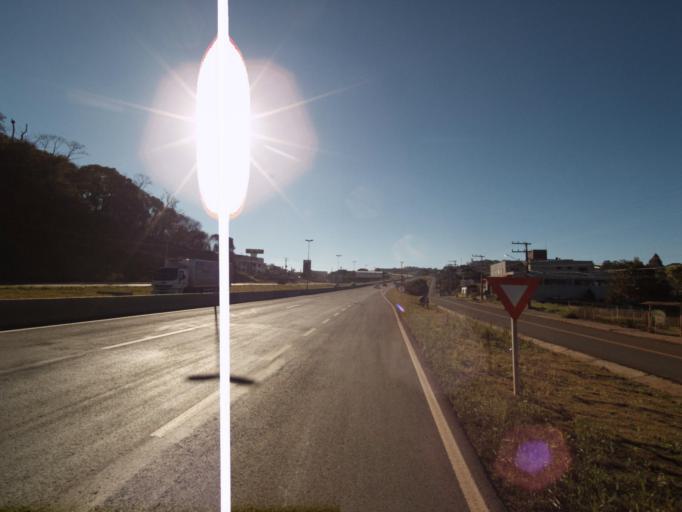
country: BR
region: Santa Catarina
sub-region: Chapeco
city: Chapeco
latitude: -27.0081
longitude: -52.6415
